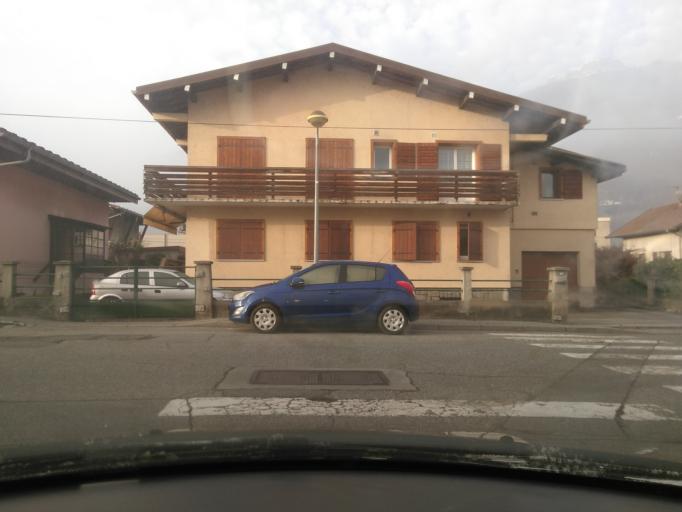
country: FR
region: Rhone-Alpes
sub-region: Departement de la Haute-Savoie
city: Sallanches
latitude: 45.9422
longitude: 6.6320
